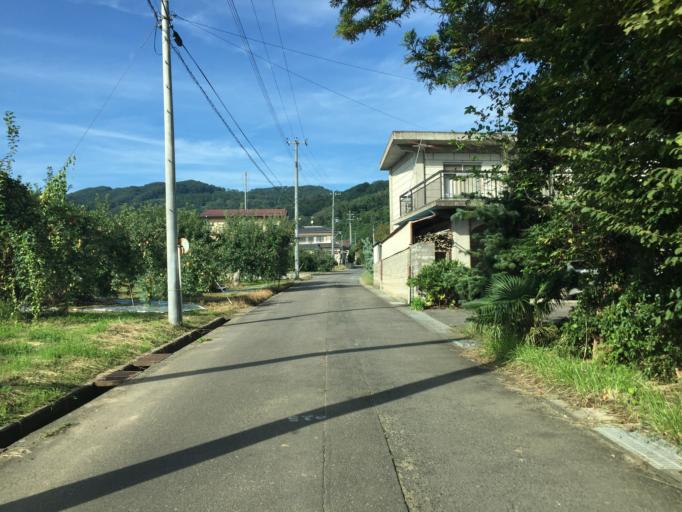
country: JP
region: Fukushima
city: Hobaramachi
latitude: 37.8391
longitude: 140.4661
